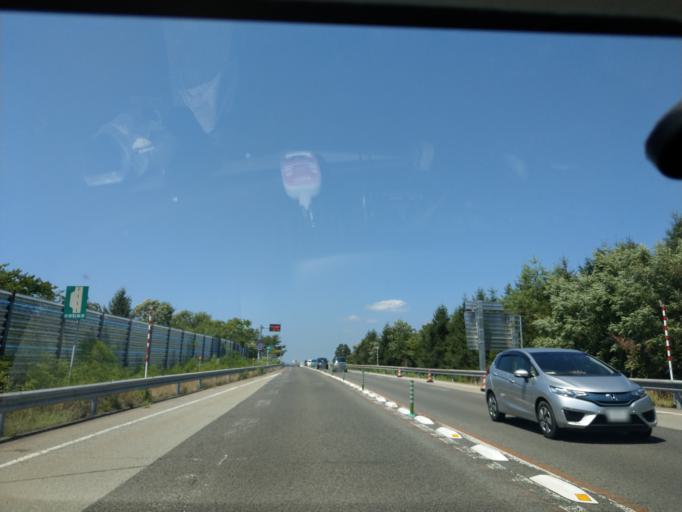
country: JP
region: Akita
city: Yokotemachi
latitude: 39.3303
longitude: 140.5088
